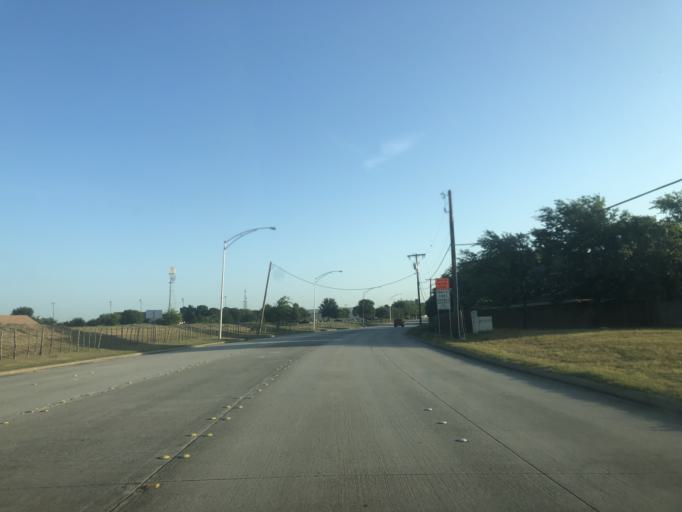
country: US
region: Texas
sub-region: Tarrant County
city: White Settlement
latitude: 32.7234
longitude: -97.5037
